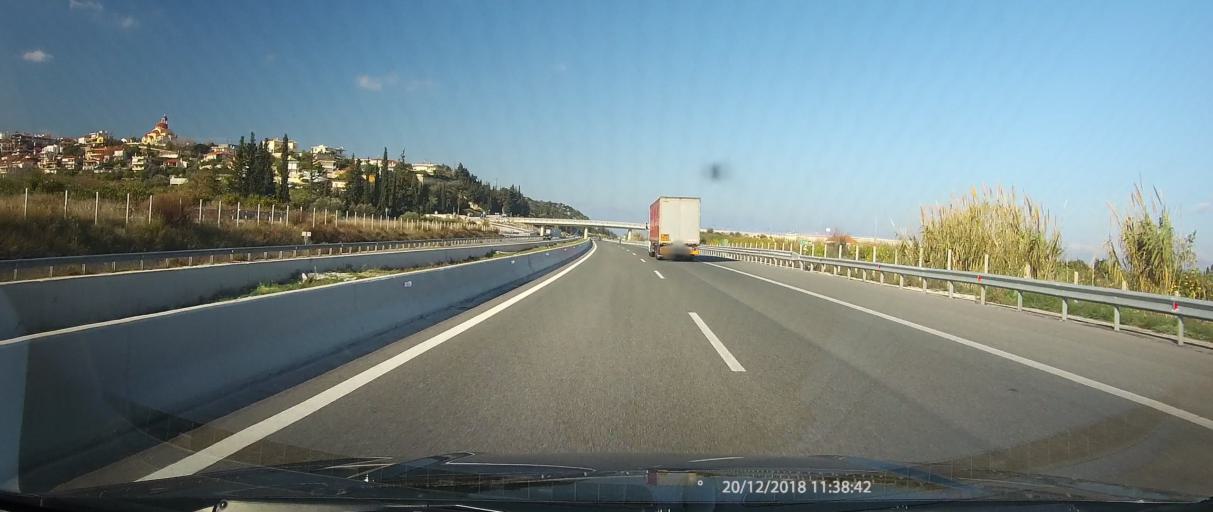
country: GR
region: Peloponnese
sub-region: Nomos Korinthias
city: Kato Dhiminio
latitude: 38.0312
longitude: 22.7192
